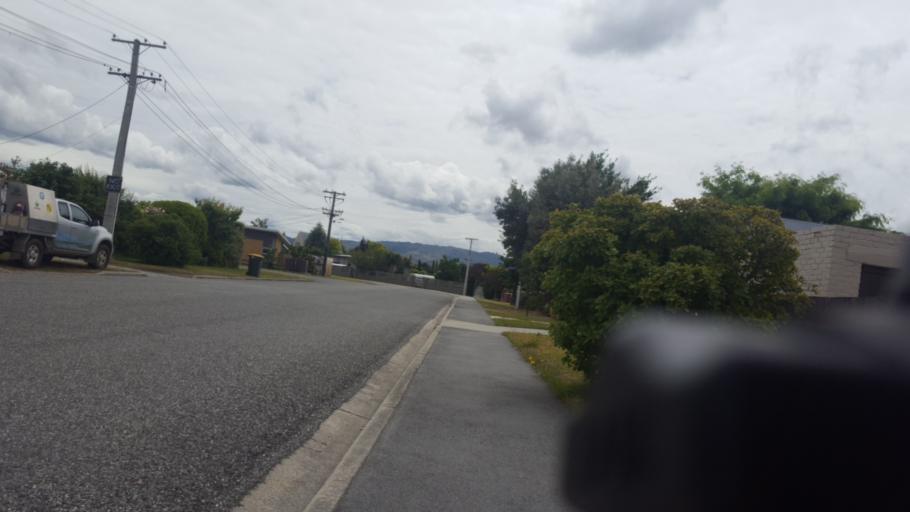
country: NZ
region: Otago
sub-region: Queenstown-Lakes District
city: Wanaka
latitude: -45.2500
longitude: 169.3805
